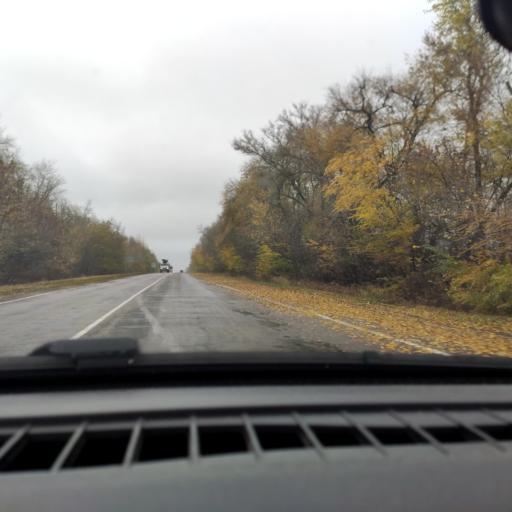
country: RU
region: Voronezj
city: Uryv-Pokrovka
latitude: 51.1434
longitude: 39.0567
